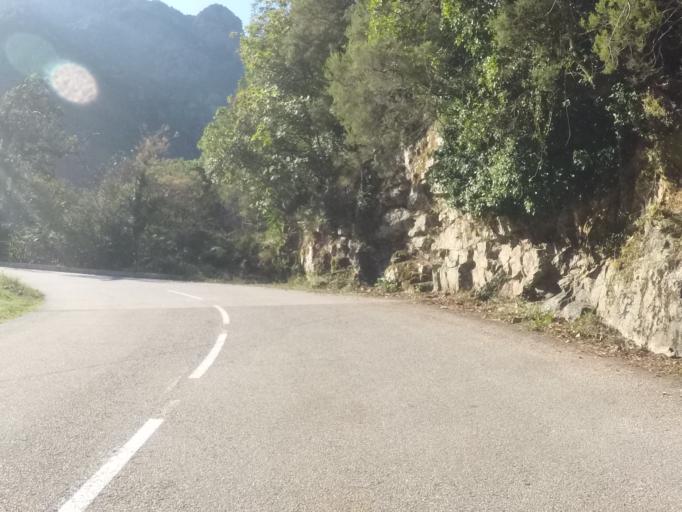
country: FR
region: Corsica
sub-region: Departement de la Corse-du-Sud
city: Cargese
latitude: 42.2416
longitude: 8.7320
